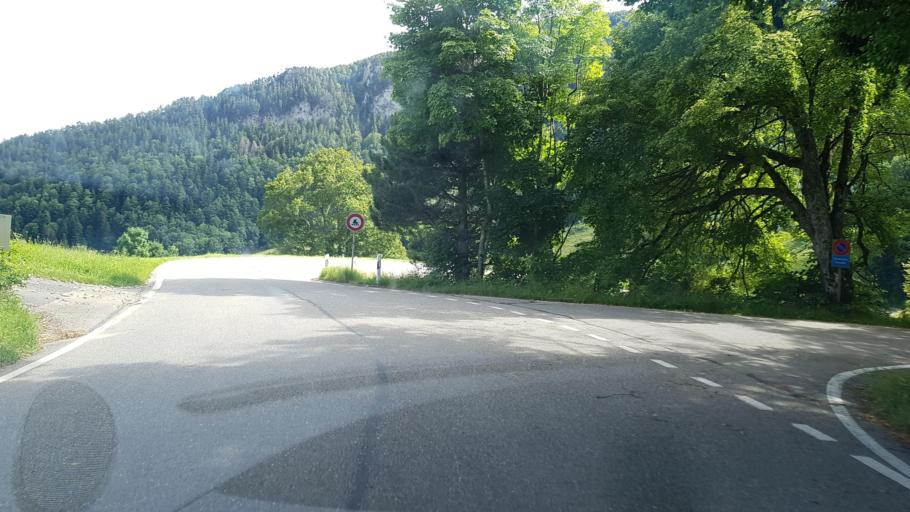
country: CH
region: Solothurn
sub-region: Bezirk Thal
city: Welschenrohr
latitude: 47.2644
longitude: 7.5403
